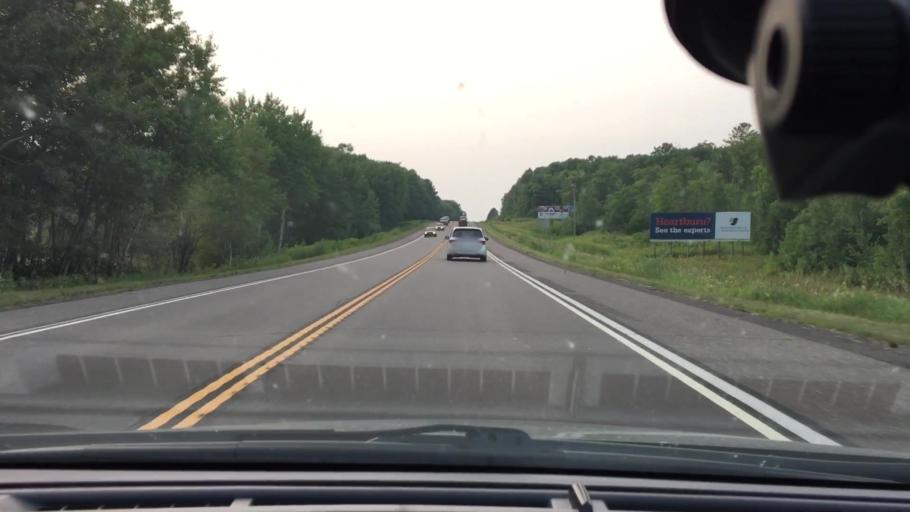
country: US
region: Minnesota
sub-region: Mille Lacs County
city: Vineland
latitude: 46.1178
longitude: -93.6640
